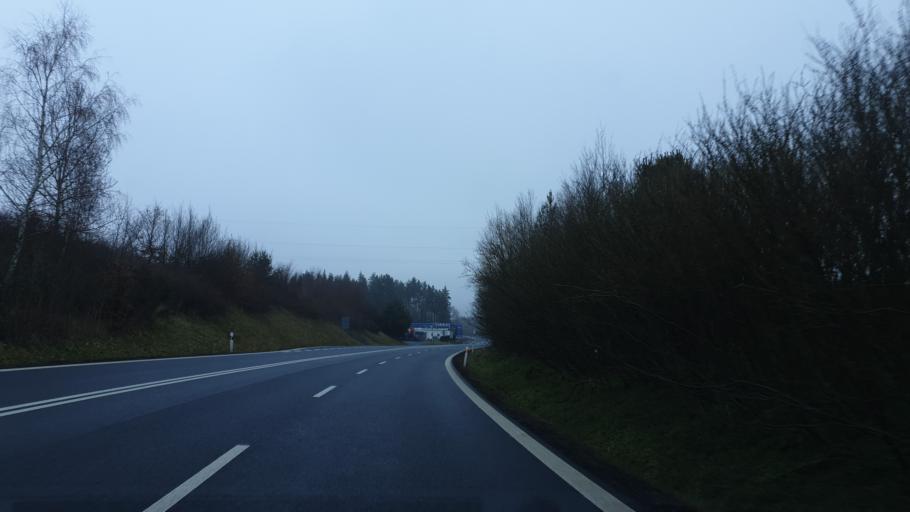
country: CZ
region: Karlovarsky
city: Hazlov
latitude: 50.1692
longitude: 12.3142
